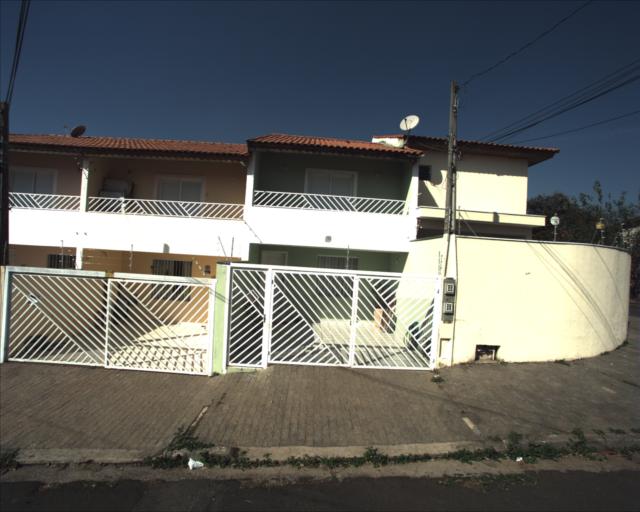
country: BR
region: Sao Paulo
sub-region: Sorocaba
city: Sorocaba
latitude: -23.4978
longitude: -47.4081
